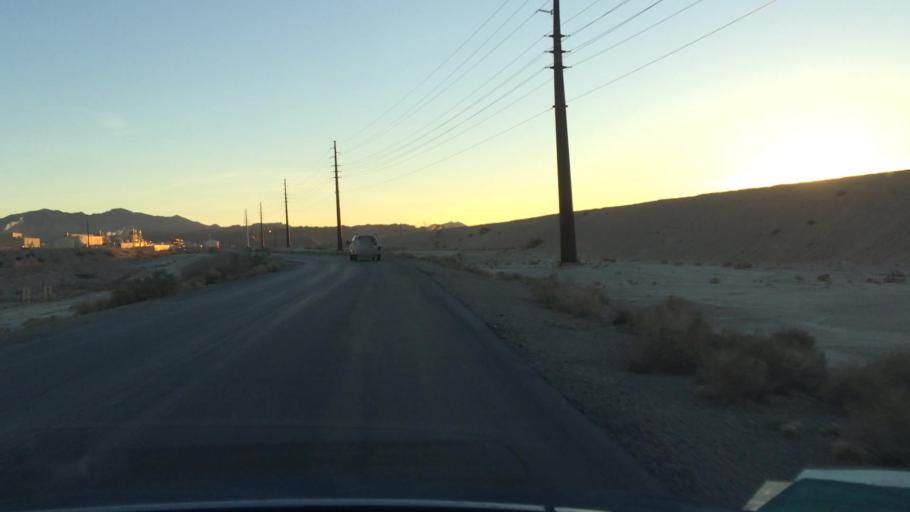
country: US
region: Nevada
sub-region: Clark County
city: Nellis Air Force Base
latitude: 36.2215
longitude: -114.8873
